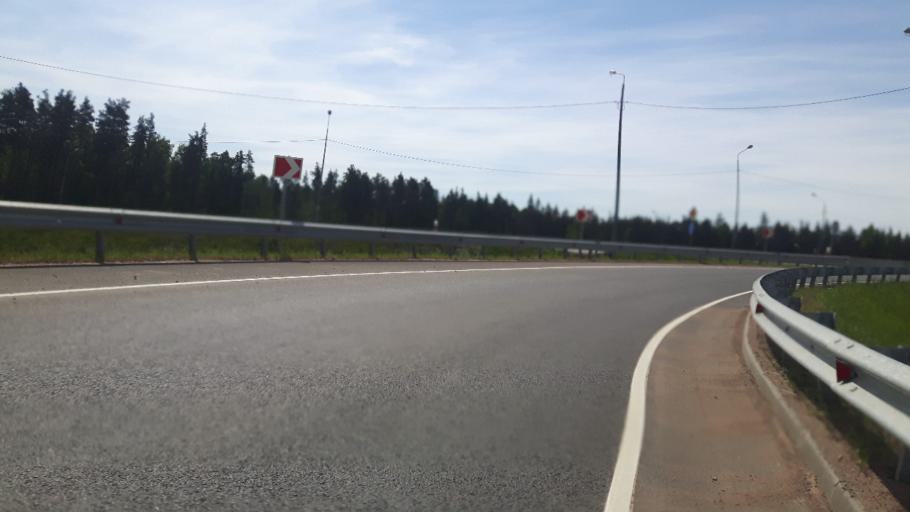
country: RU
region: Leningrad
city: Vistino
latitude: 59.6628
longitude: 28.4406
